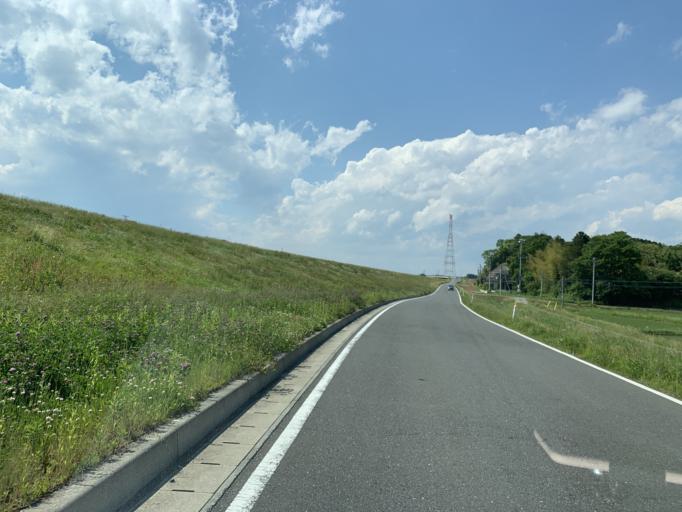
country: JP
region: Miyagi
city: Matsushima
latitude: 38.4248
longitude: 141.1277
